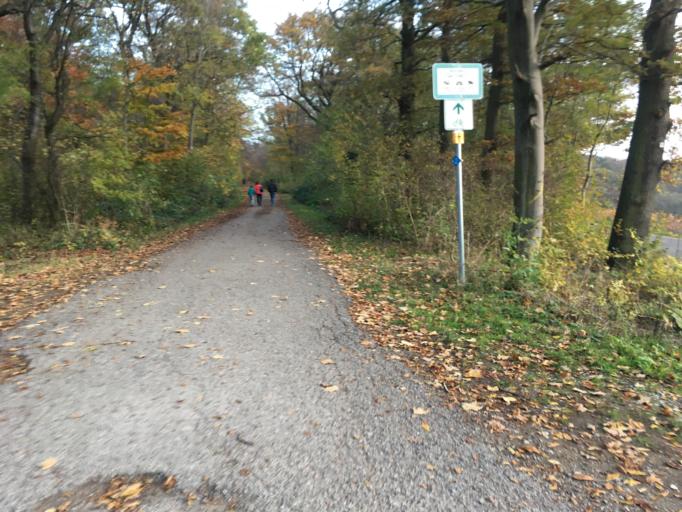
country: DE
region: Baden-Wuerttemberg
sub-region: Regierungsbezirk Stuttgart
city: Weinsberg
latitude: 49.1461
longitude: 9.2633
